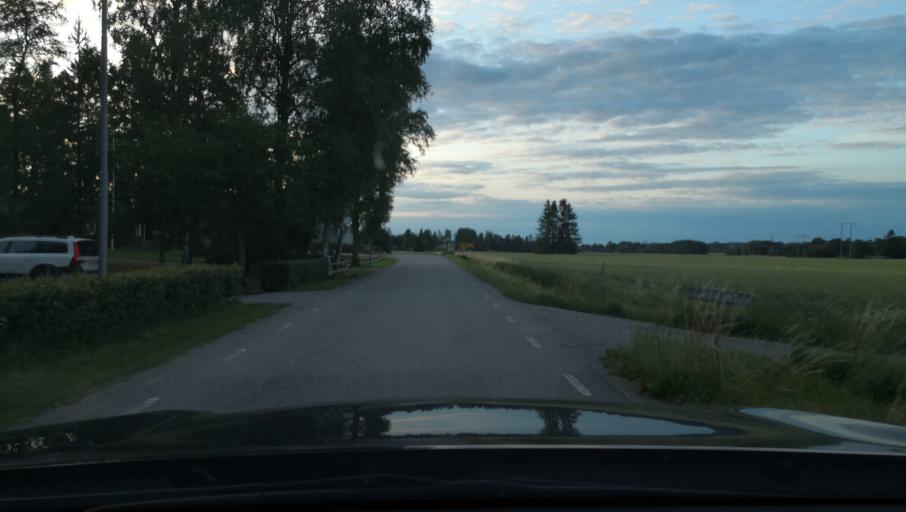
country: SE
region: Uppsala
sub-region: Uppsala Kommun
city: Storvreta
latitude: 60.0246
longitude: 17.6645
